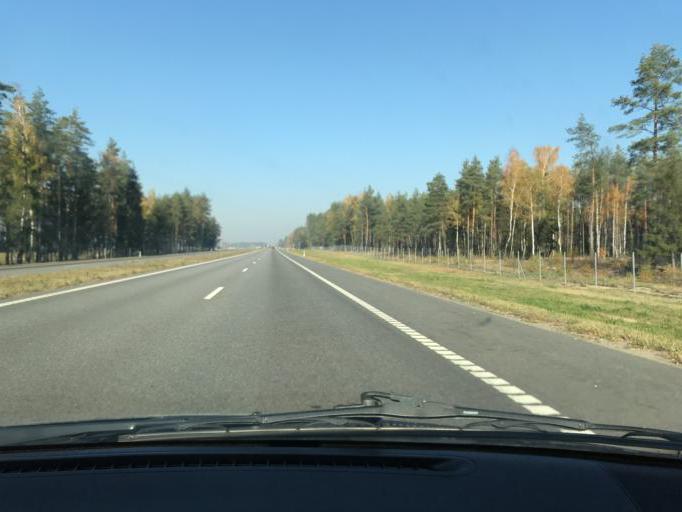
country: BY
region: Minsk
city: Slutsk
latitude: 53.3097
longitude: 27.5396
